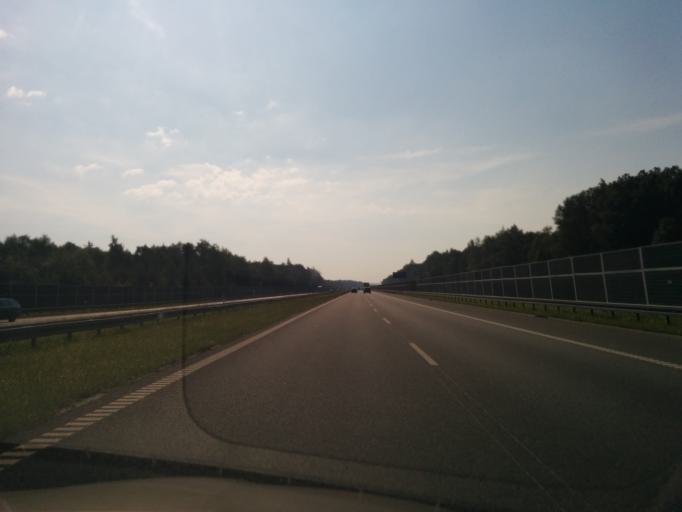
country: PL
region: Silesian Voivodeship
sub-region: Powiat tarnogorski
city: Radzionkow
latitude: 50.3860
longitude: 18.8511
